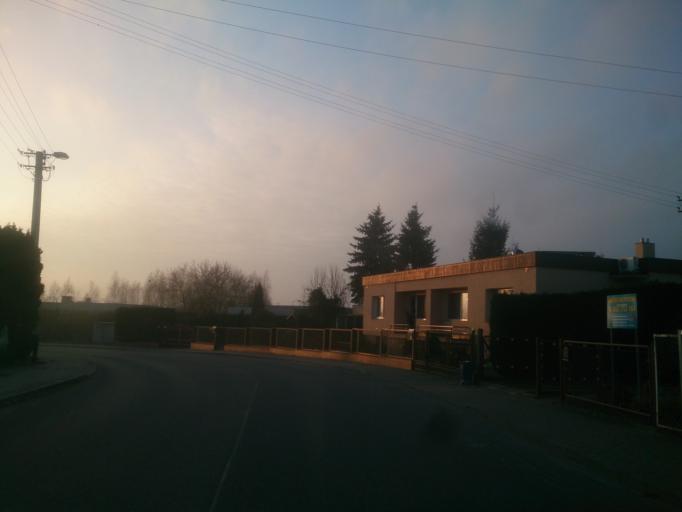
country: PL
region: Kujawsko-Pomorskie
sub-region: Powiat brodnicki
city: Brodnica
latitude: 53.2594
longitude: 19.3793
